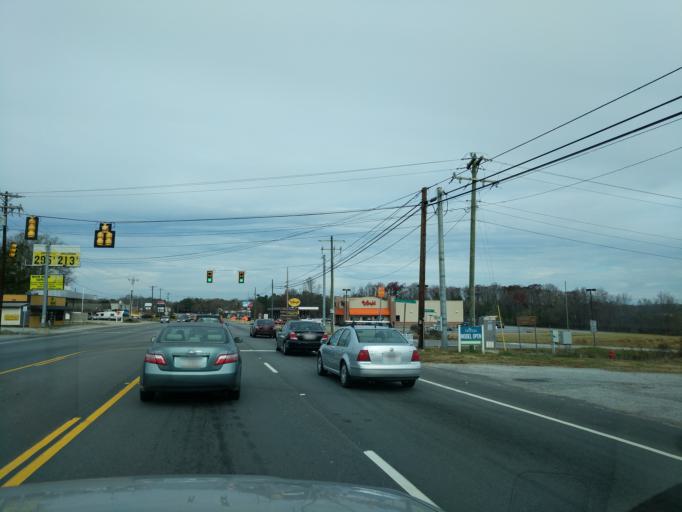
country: US
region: South Carolina
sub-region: Anderson County
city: Pendleton
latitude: 34.6302
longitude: -82.7818
